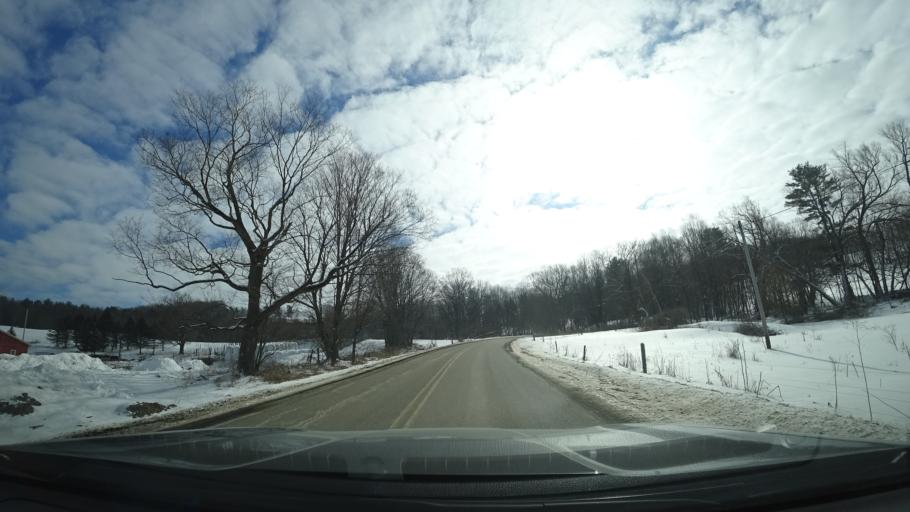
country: US
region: New York
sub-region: Washington County
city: Fort Edward
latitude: 43.2452
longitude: -73.4498
